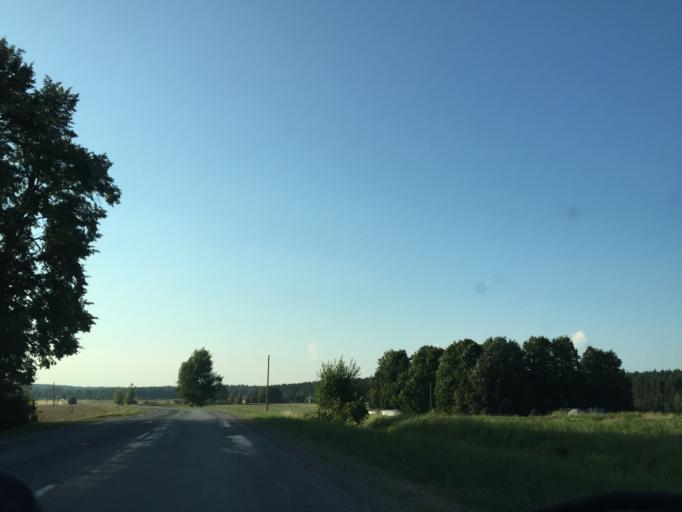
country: LV
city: Tervete
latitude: 56.4675
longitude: 23.4017
